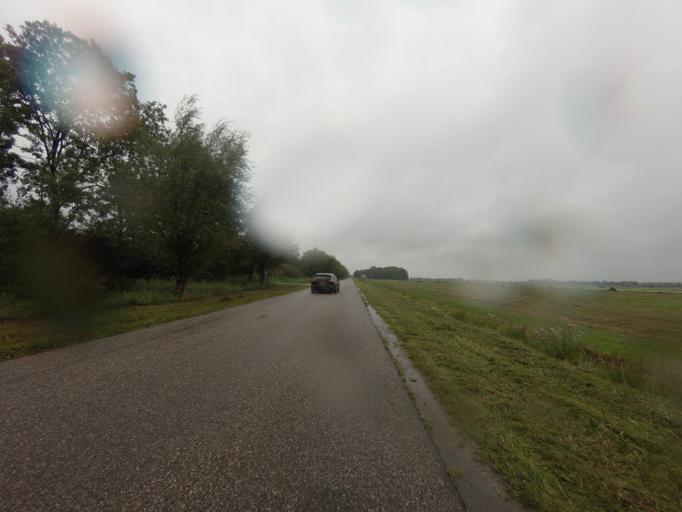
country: NL
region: Friesland
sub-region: Gemeente Tytsjerksteradiel
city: Garyp
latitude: 53.1325
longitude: 5.9576
